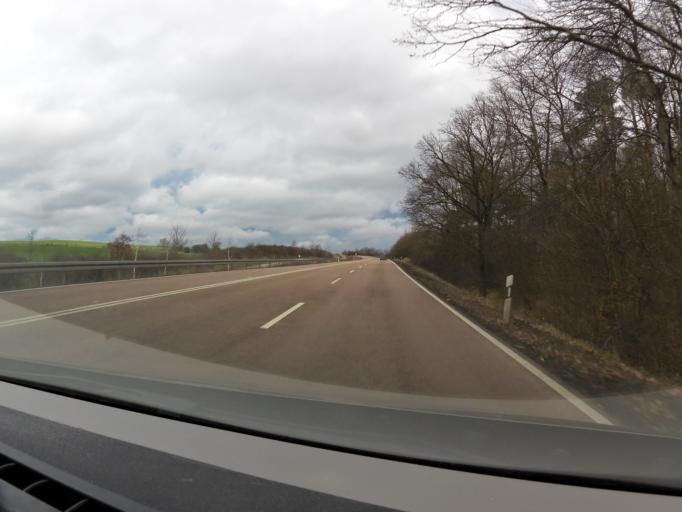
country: DE
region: Saxony-Anhalt
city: Riestedt
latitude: 51.5106
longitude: 11.3734
